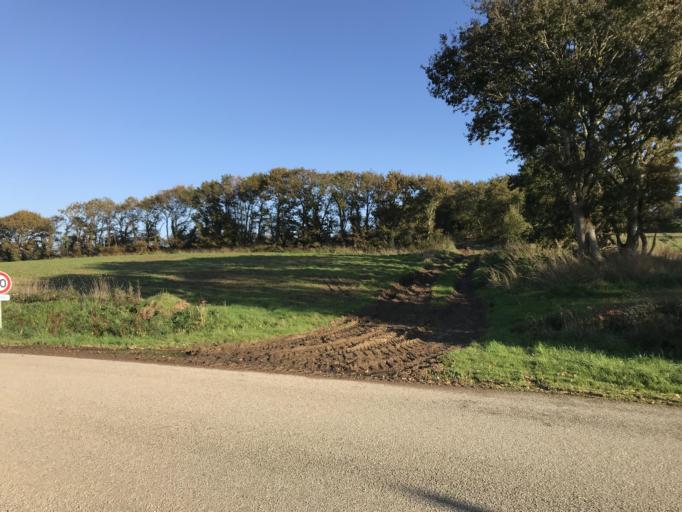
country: FR
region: Brittany
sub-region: Departement du Finistere
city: Hopital-Camfrout
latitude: 48.3072
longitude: -4.2316
